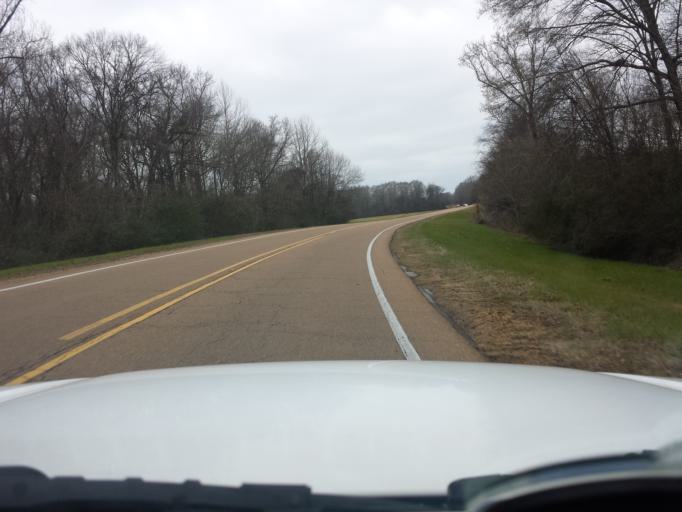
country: US
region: Mississippi
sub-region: Madison County
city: Canton
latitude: 32.7350
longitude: -90.1150
